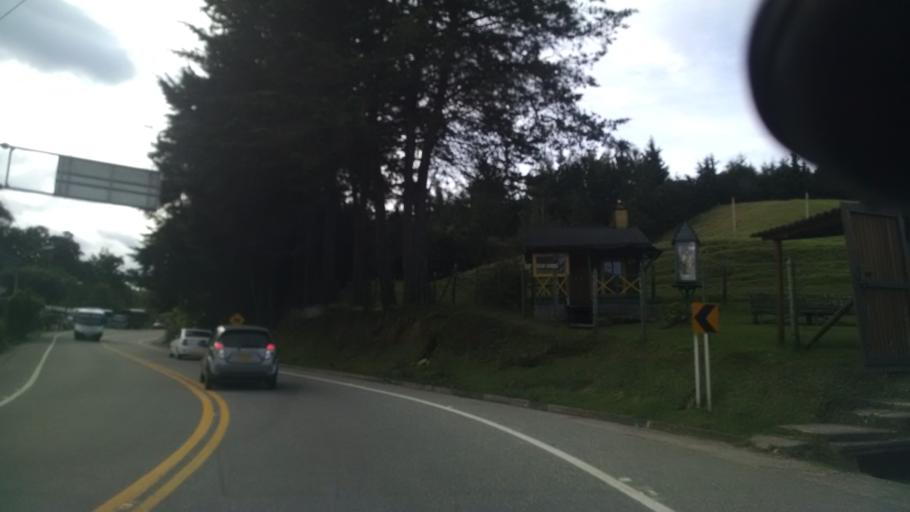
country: CO
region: Antioquia
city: Envigado
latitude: 6.1439
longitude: -75.5242
